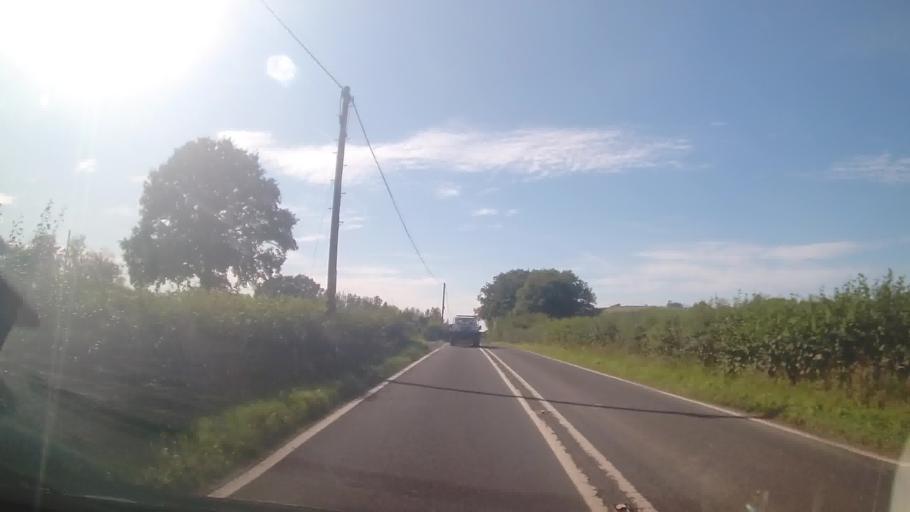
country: GB
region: Wales
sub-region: Sir Powys
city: Llandrindod Wells
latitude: 52.2828
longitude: -3.3824
